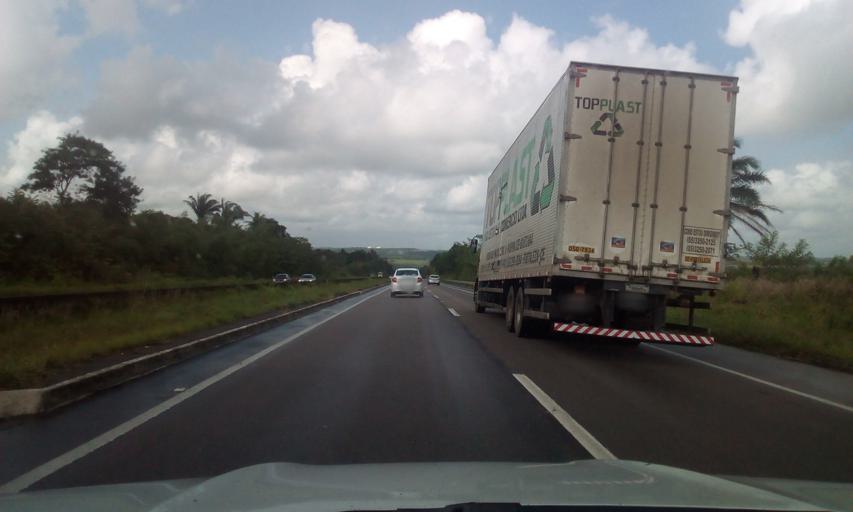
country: BR
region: Paraiba
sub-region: Alhandra
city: Alhandra
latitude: -7.3662
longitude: -34.9532
